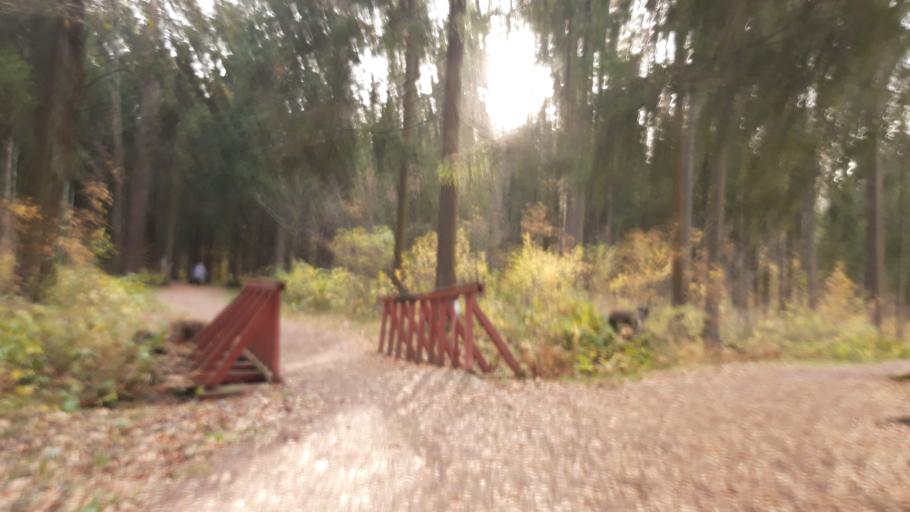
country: RU
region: Moscow
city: Zelenograd
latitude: 56.0010
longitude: 37.1792
